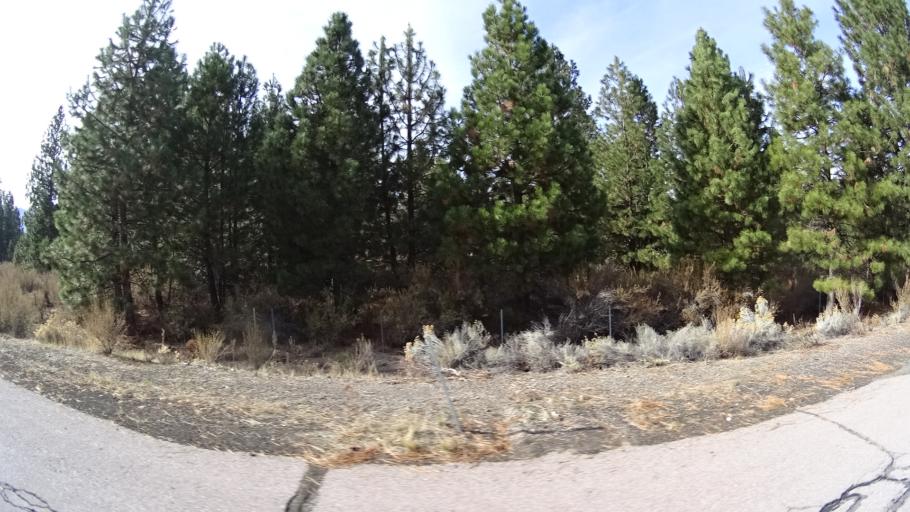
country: US
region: California
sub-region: Siskiyou County
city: Weed
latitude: 41.3979
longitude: -122.3831
